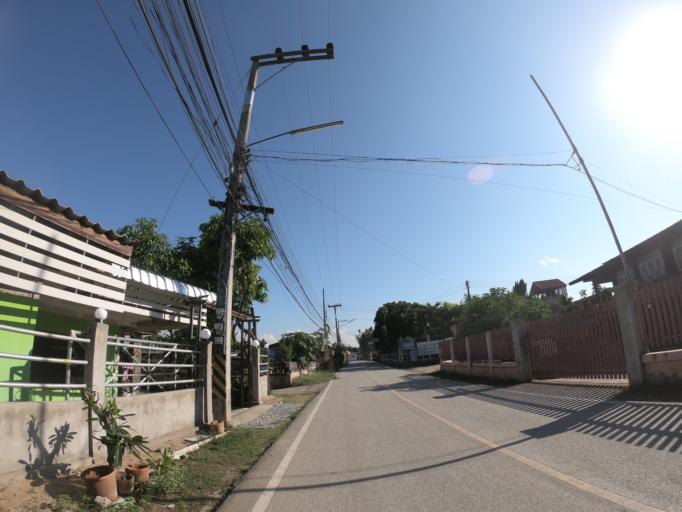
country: TH
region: Chiang Mai
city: Saraphi
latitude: 18.7040
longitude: 98.9876
